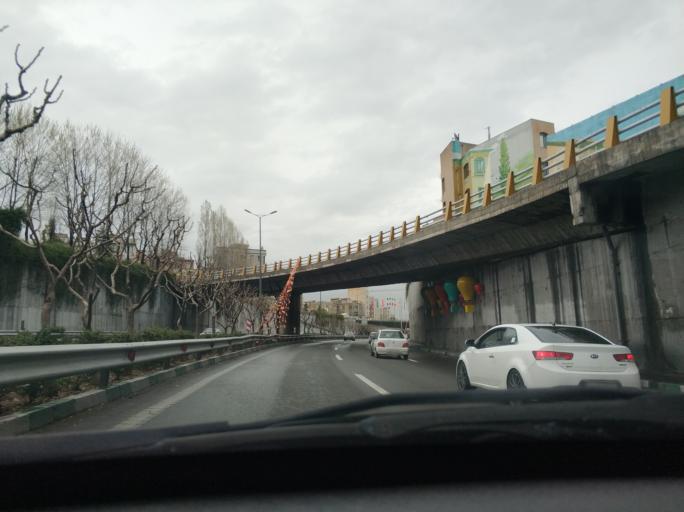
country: IR
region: Tehran
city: Tehran
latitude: 35.7206
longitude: 51.4488
